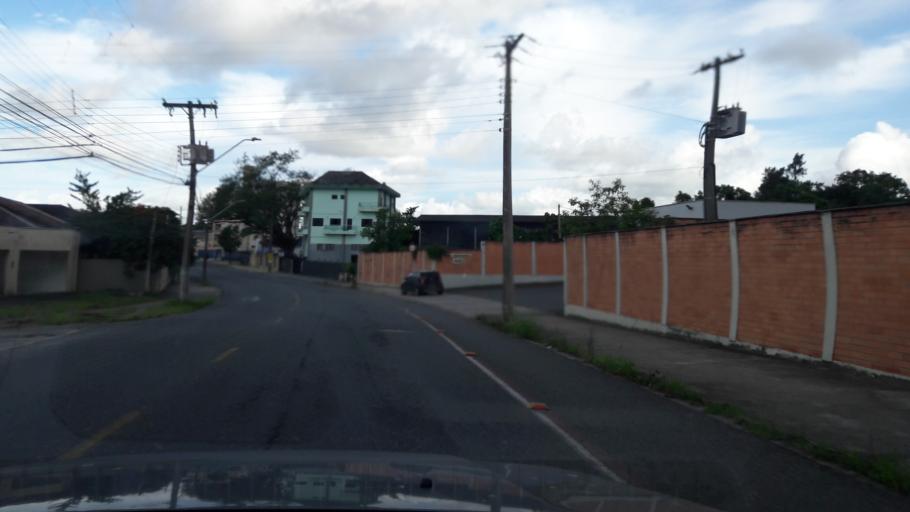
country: BR
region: Santa Catarina
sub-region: Joinville
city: Joinville
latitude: -26.3252
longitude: -48.8345
